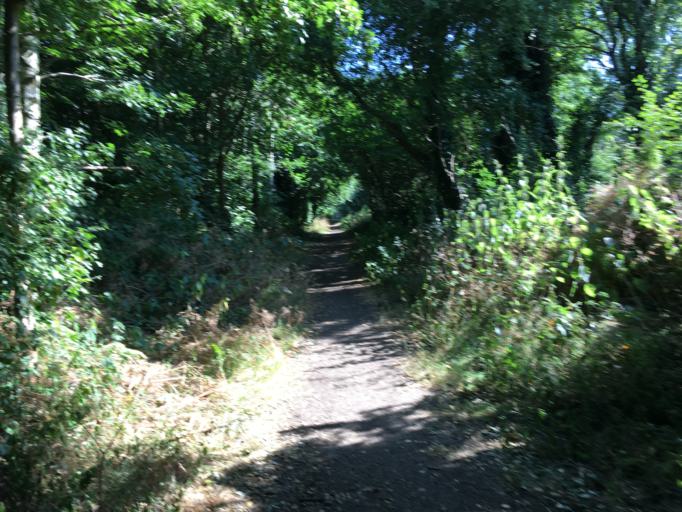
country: GB
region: England
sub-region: Warwickshire
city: Rugby
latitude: 52.3900
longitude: -1.2373
